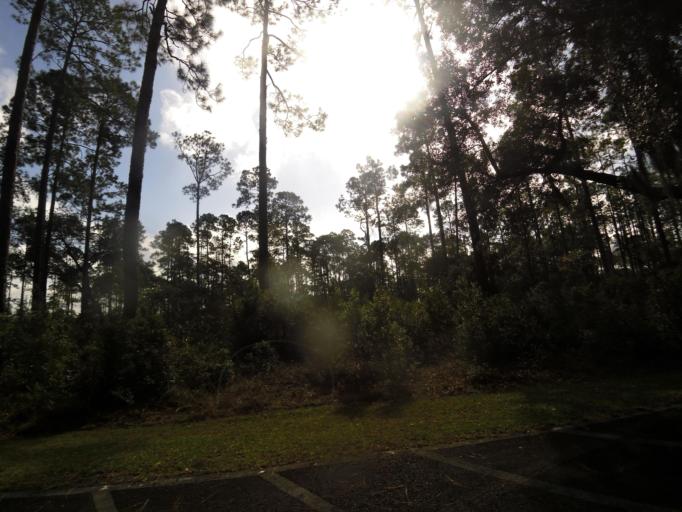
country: US
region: Georgia
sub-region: Charlton County
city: Folkston
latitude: 30.7138
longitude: -82.1554
